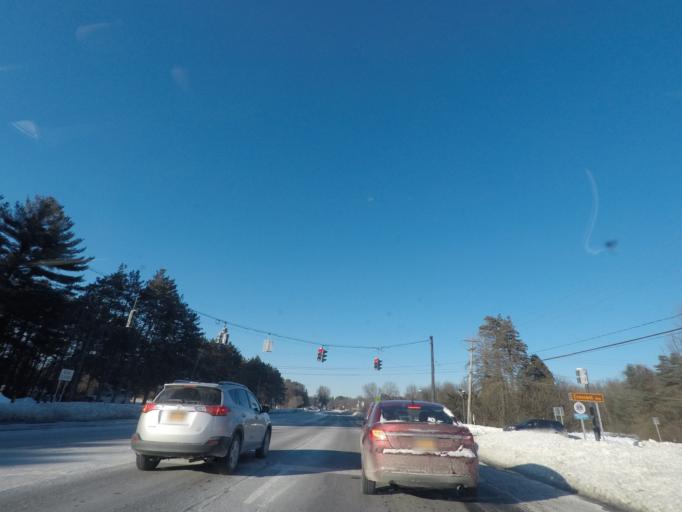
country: US
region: New York
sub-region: Saratoga County
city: Saratoga Springs
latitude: 43.0584
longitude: -73.7877
